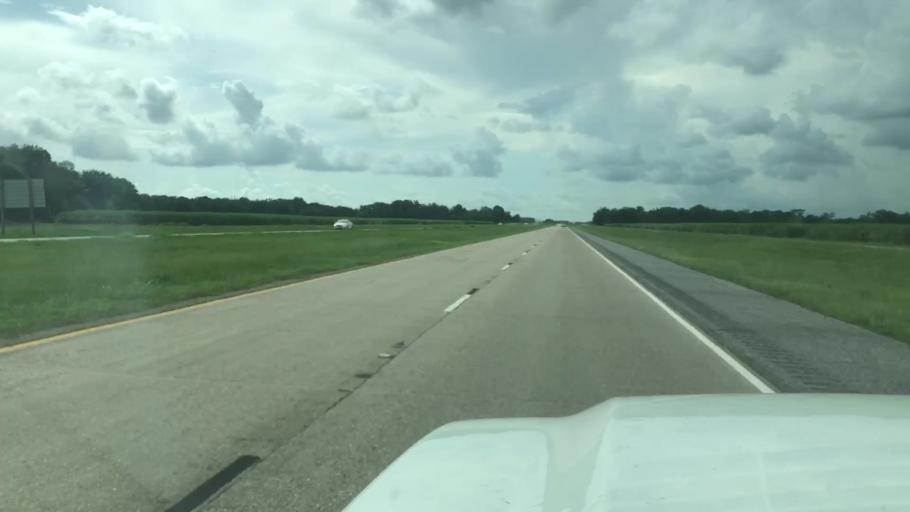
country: US
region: Louisiana
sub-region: Saint Mary Parish
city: Franklin
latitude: 29.7611
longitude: -91.4792
